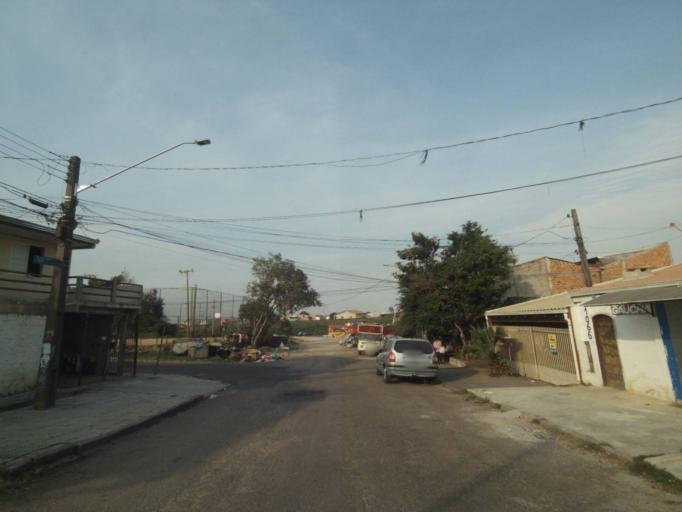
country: BR
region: Parana
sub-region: Sao Jose Dos Pinhais
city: Sao Jose dos Pinhais
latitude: -25.4918
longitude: -49.2035
